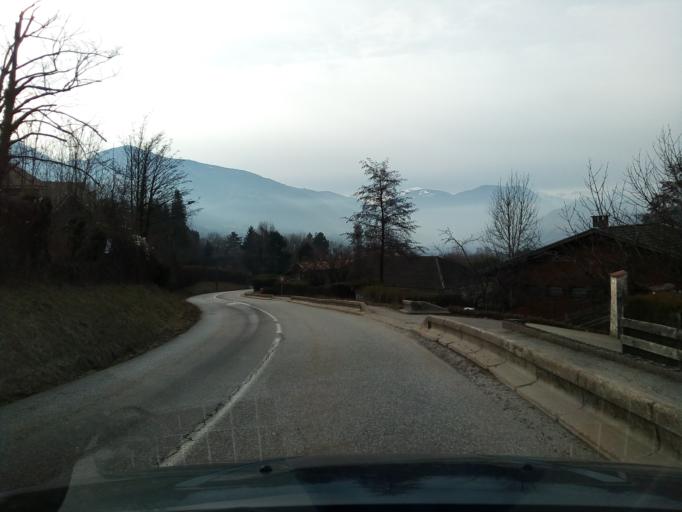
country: FR
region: Rhone-Alpes
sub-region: Departement de l'Isere
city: Vaulnaveys-le-Haut
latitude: 45.1469
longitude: 5.8372
